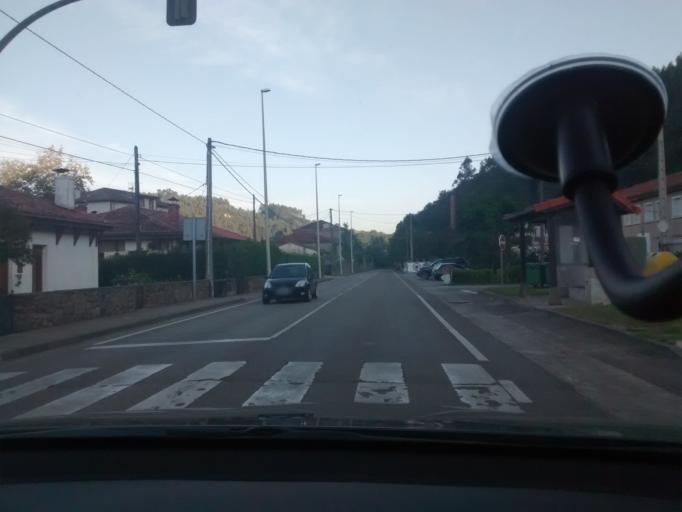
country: ES
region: Cantabria
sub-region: Provincia de Cantabria
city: Entrambasaguas
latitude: 43.3593
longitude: -3.7111
